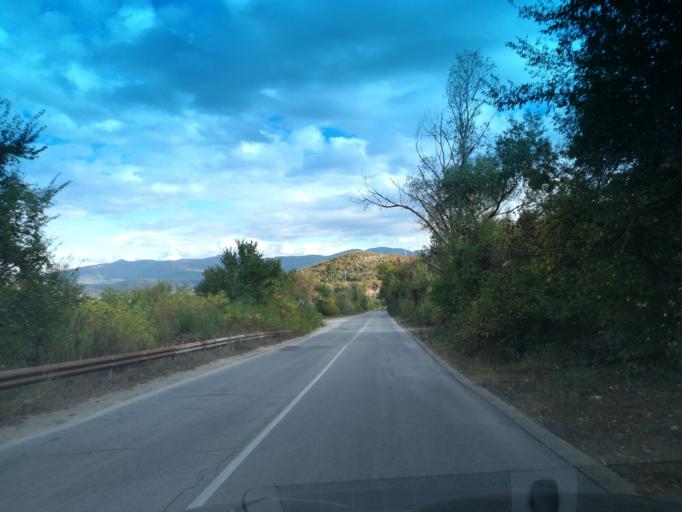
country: BG
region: Pazardzhik
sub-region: Obshtina Peshtera
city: Peshtera
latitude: 42.0485
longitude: 24.3260
